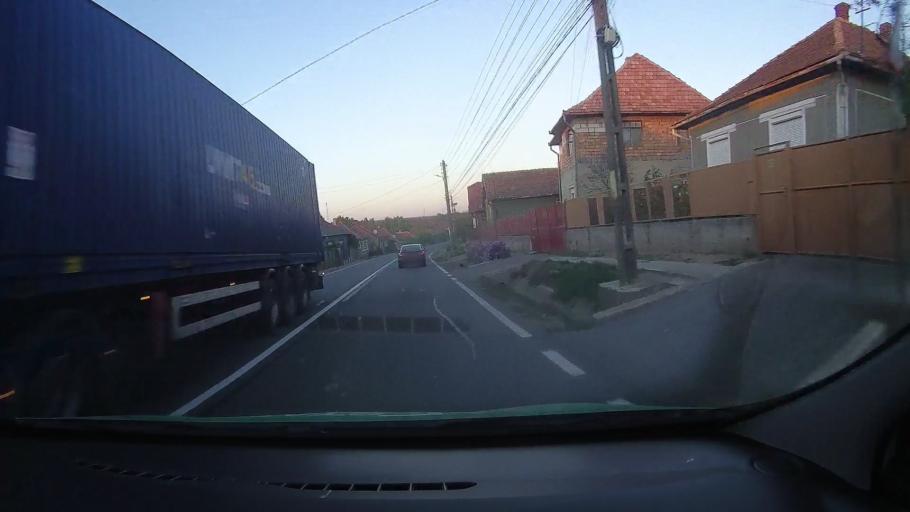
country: RO
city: Szekelyhid
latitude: 47.3546
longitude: 22.1092
